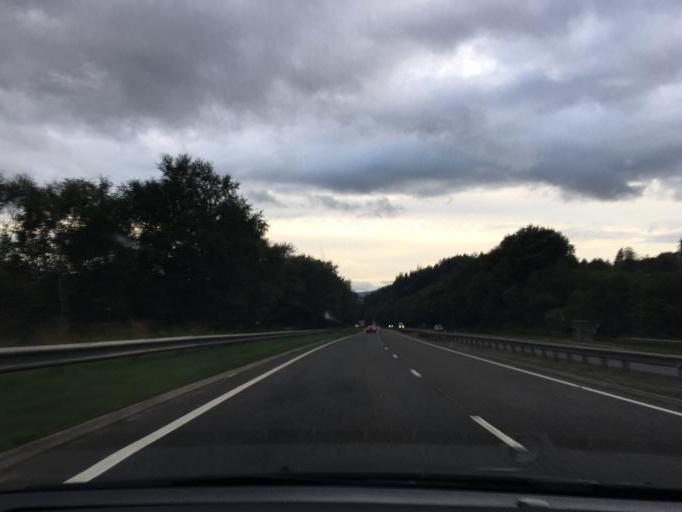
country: GB
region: Scotland
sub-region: Highland
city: Inverness
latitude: 57.4257
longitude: -4.1272
